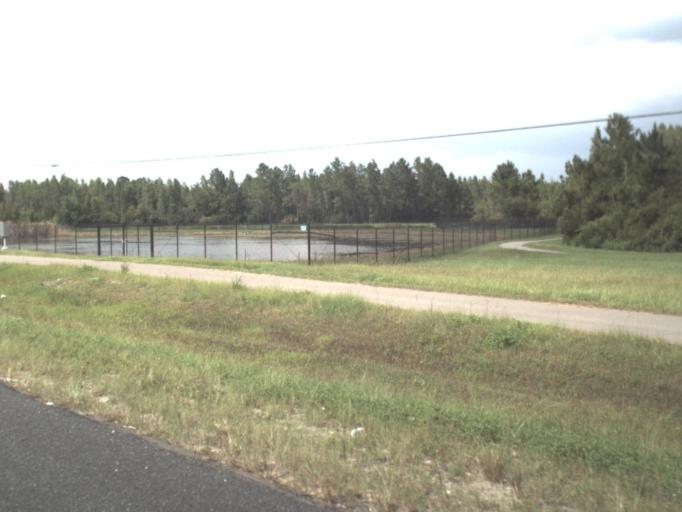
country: US
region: Florida
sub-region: Pasco County
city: Land O' Lakes
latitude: 28.2833
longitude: -82.4857
